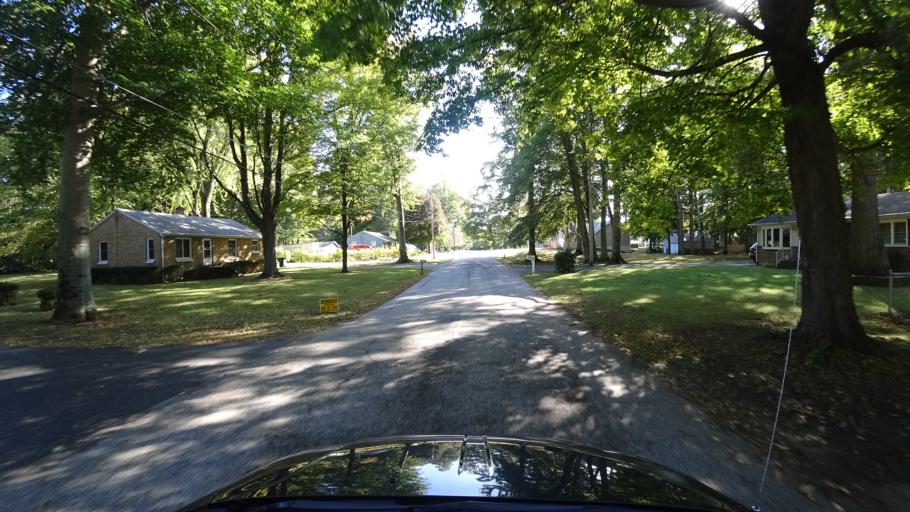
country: US
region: Indiana
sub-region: LaPorte County
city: Trail Creek
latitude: 41.7082
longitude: -86.8514
